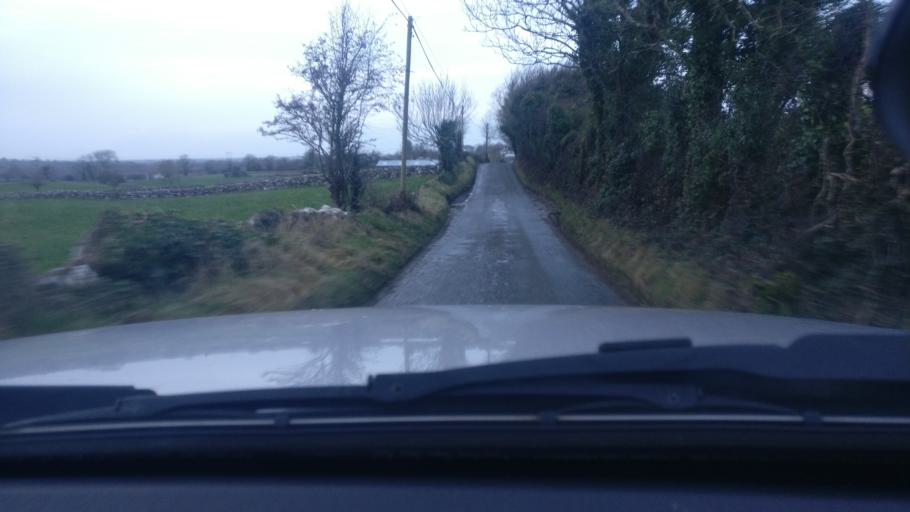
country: IE
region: Connaught
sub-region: County Galway
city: Loughrea
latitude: 53.1772
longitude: -8.5895
